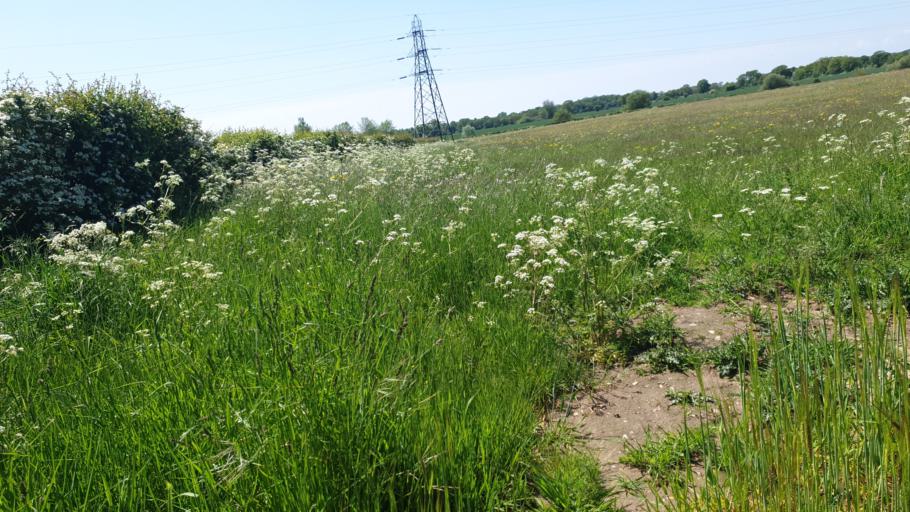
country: GB
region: England
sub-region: Essex
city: Manningtree
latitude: 51.9056
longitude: 1.0381
